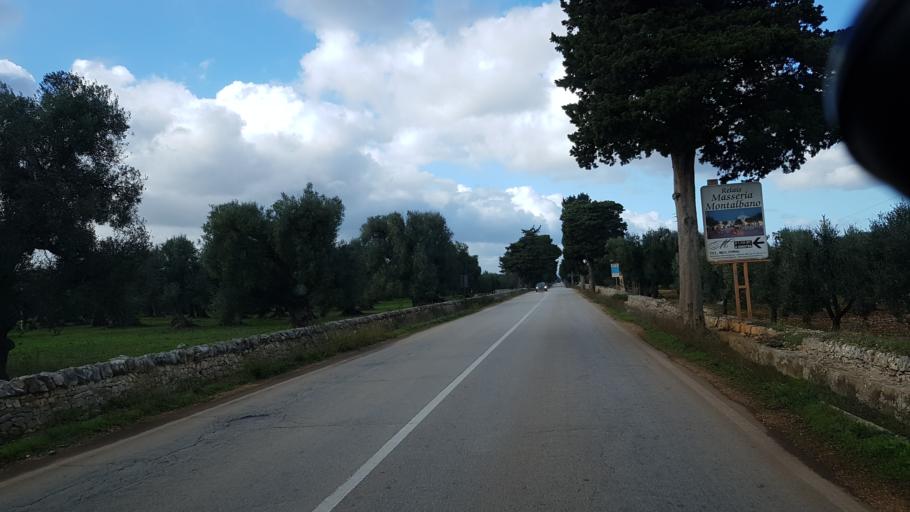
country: IT
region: Apulia
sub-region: Provincia di Brindisi
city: Montalbano
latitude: 40.7680
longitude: 17.5124
